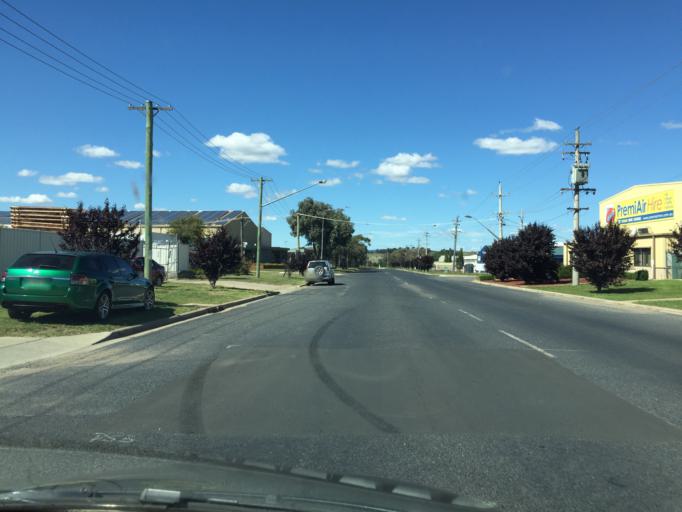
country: AU
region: Australian Capital Territory
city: Macarthur
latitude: -35.3872
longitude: 149.1722
